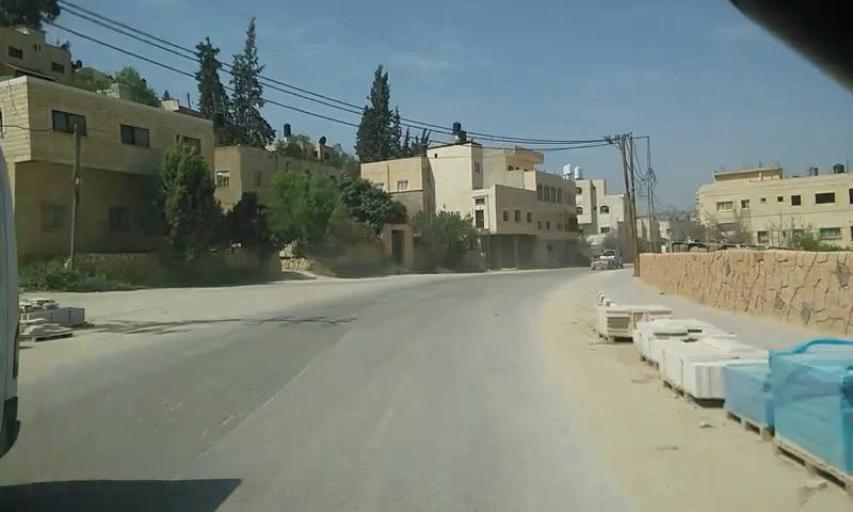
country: PS
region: West Bank
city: Qabatiyah
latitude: 32.4063
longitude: 35.2884
